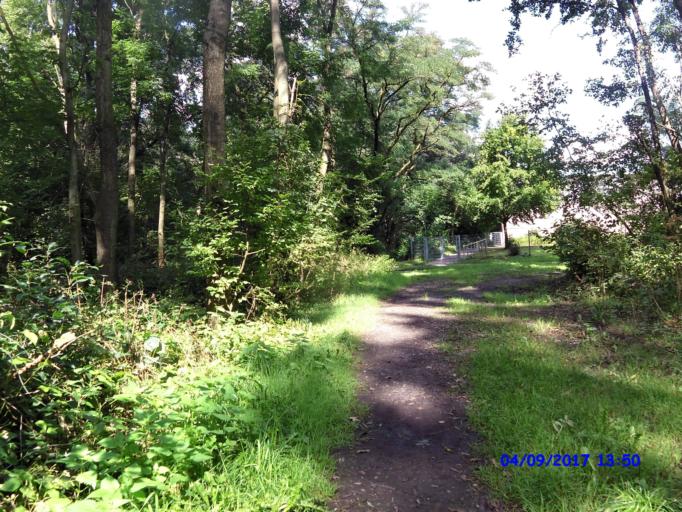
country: DE
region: Saxony
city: Taucha
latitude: 51.3561
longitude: 12.4683
